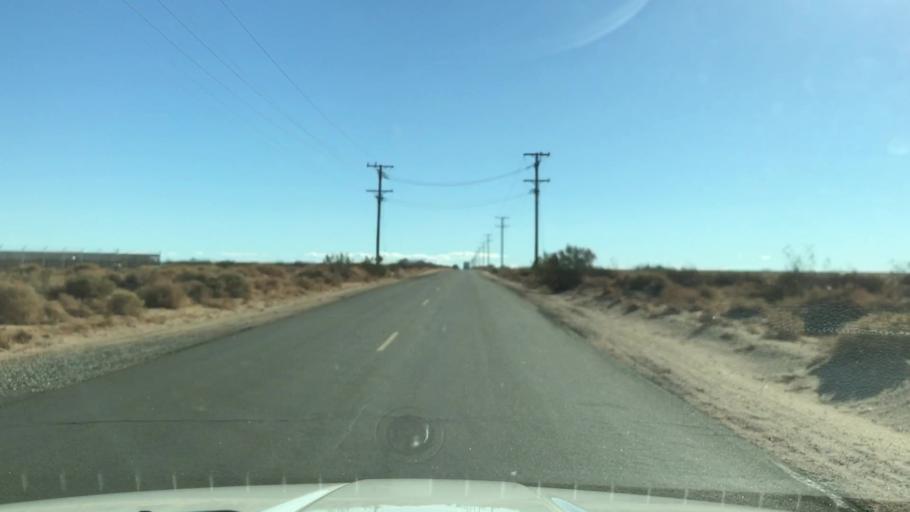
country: US
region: California
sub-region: Kern County
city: California City
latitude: 35.2432
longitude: -117.9860
